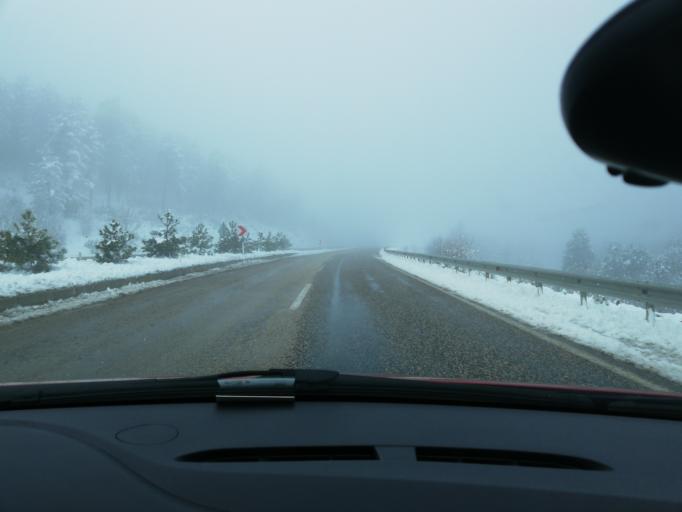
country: TR
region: Kastamonu
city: Akkaya
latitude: 41.2975
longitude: 33.5108
